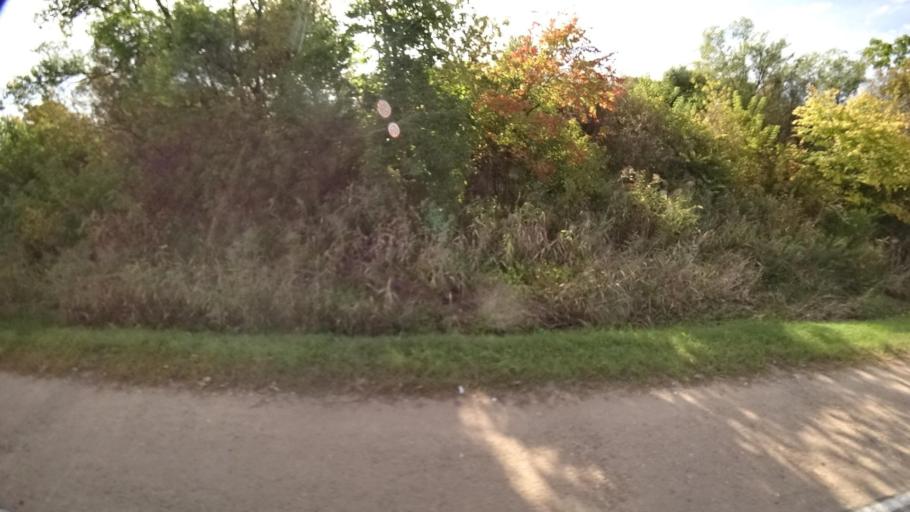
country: RU
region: Primorskiy
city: Dostoyevka
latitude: 44.2942
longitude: 133.4264
